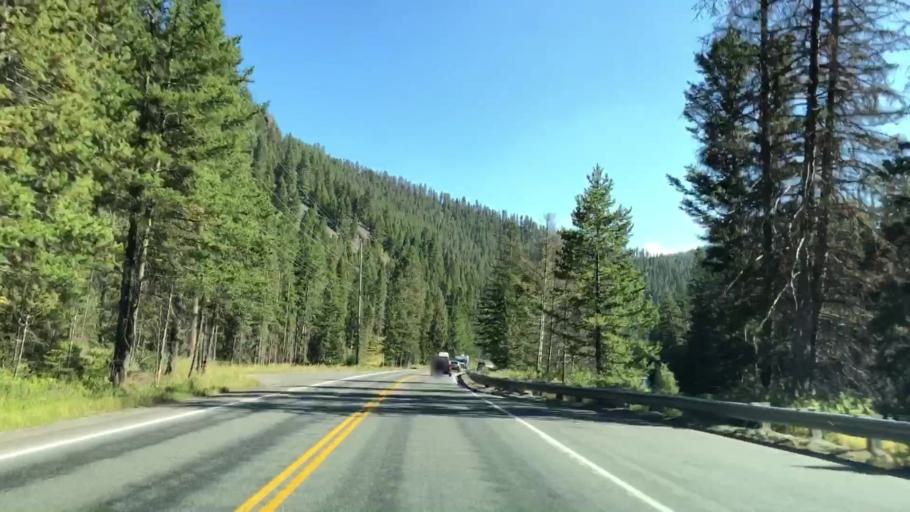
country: US
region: Montana
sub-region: Gallatin County
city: Big Sky
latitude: 45.3634
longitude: -111.1730
